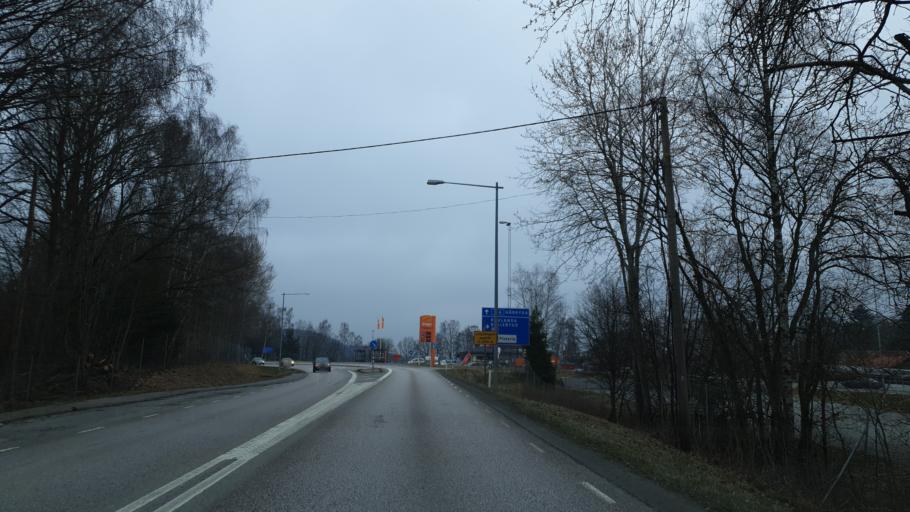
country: SE
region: Vaestra Goetaland
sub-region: Harryda Kommun
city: Ravlanda
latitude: 57.6180
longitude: 12.4347
